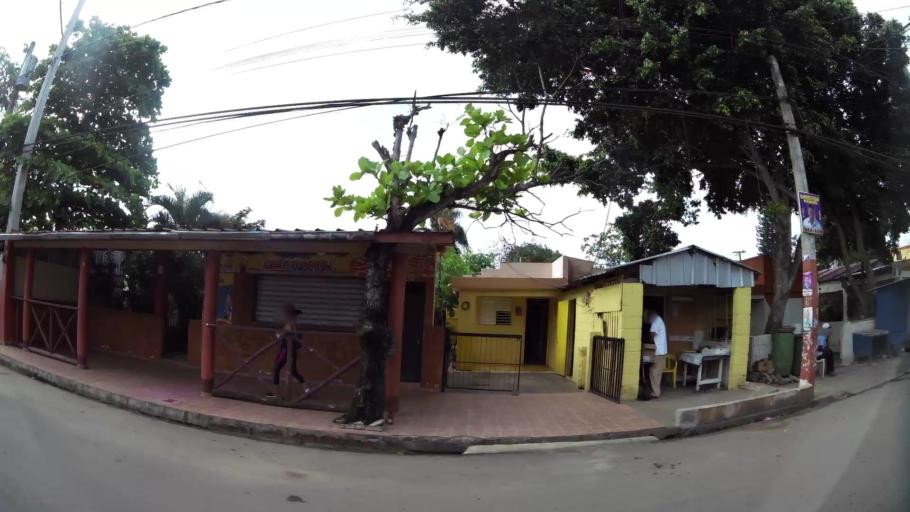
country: DO
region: Santiago
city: Santiago de los Caballeros
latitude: 19.4263
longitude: -70.6556
